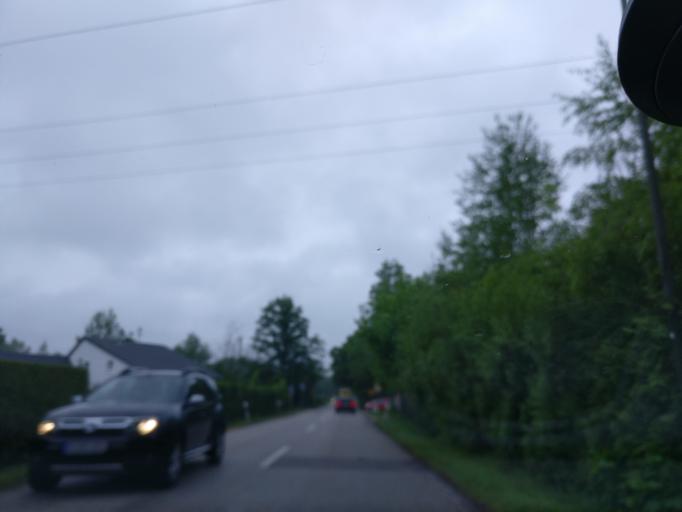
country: DE
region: Bavaria
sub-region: Upper Bavaria
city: Grobenzell
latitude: 48.2021
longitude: 11.4061
